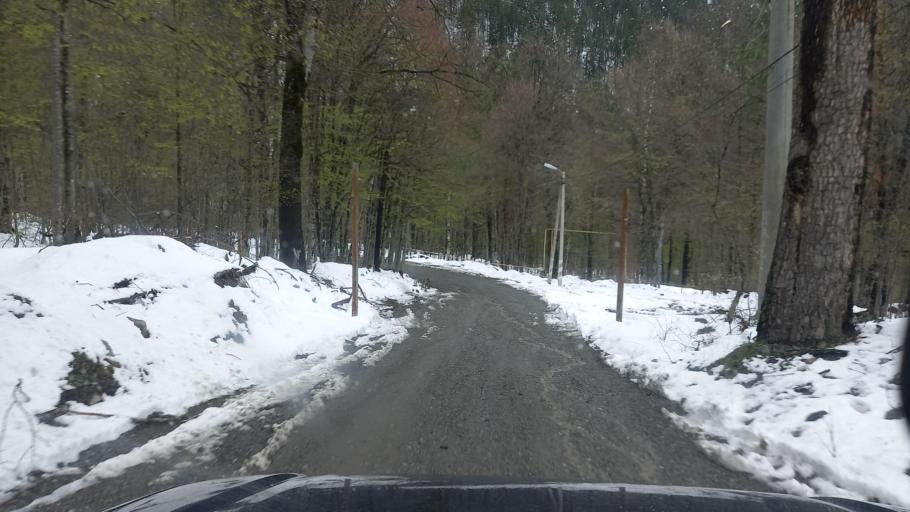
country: RU
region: North Ossetia
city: Mizur
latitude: 42.7875
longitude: 43.9031
